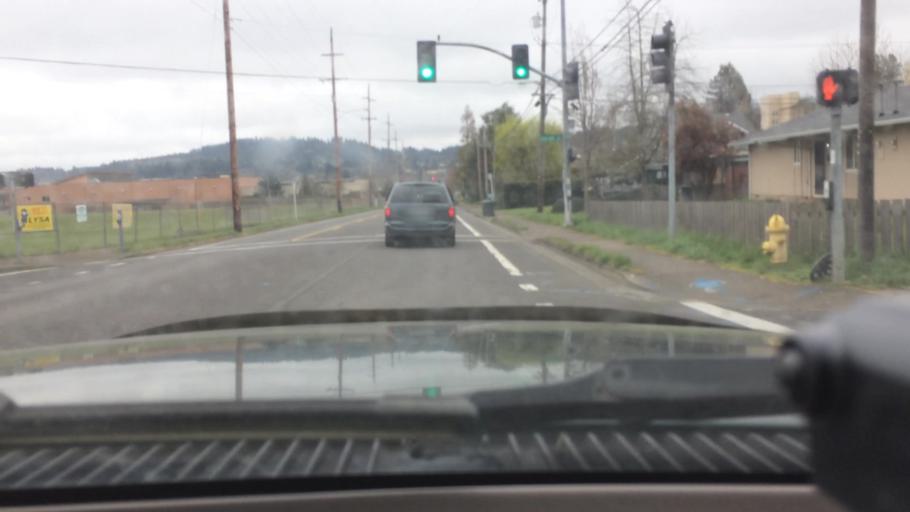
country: US
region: Oregon
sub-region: Lane County
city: Eugene
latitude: 44.0262
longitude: -123.0973
